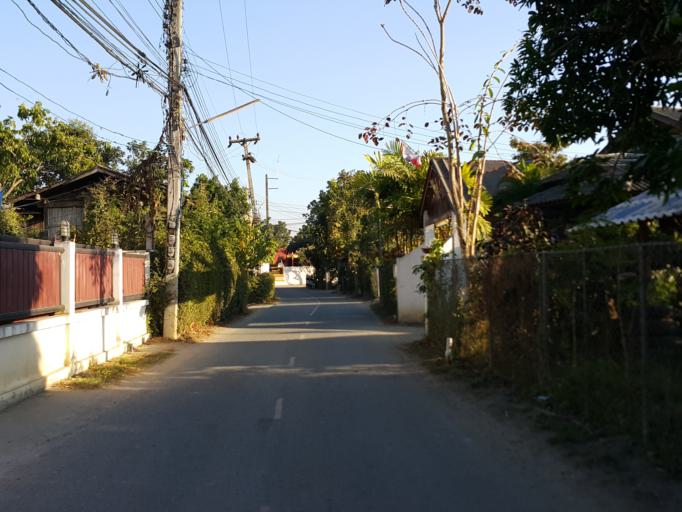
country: TH
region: Chiang Mai
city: San Kamphaeng
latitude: 18.7909
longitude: 99.1084
